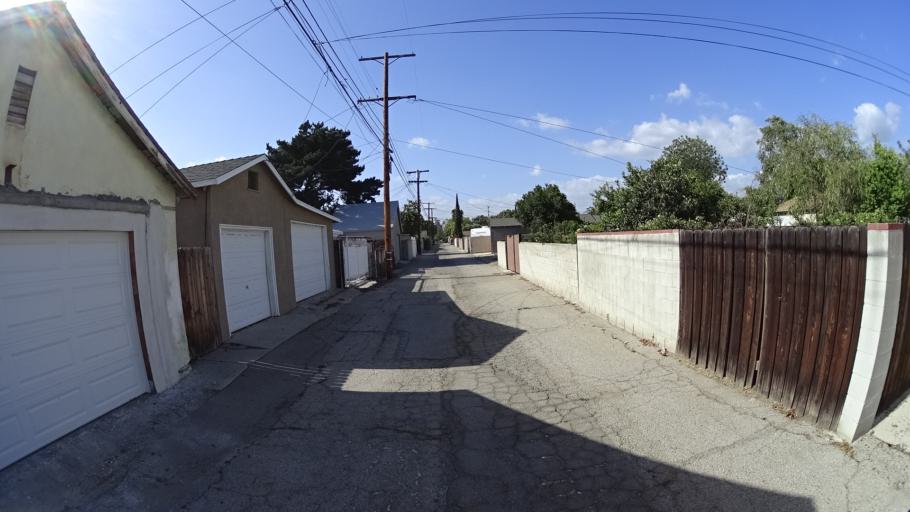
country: US
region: California
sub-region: Los Angeles County
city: North Hollywood
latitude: 34.1739
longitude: -118.3575
